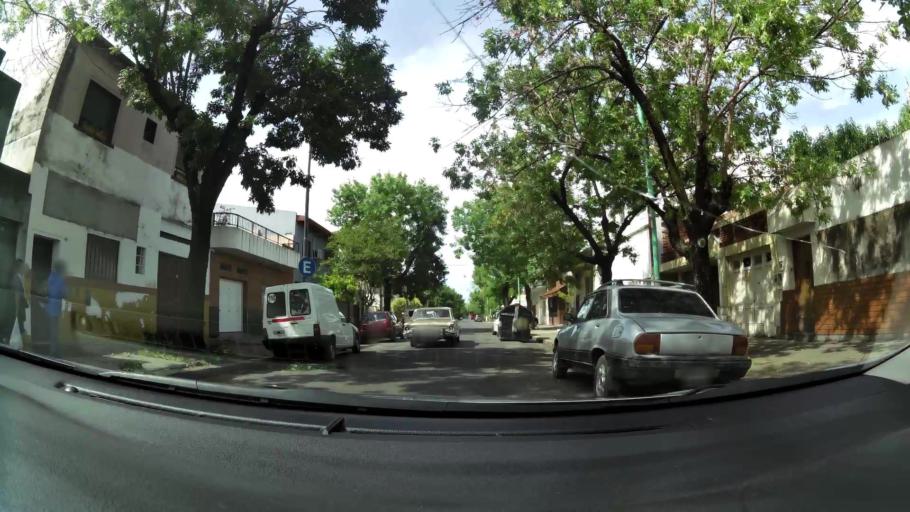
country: AR
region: Buenos Aires F.D.
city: Villa Lugano
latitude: -34.6564
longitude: -58.4279
